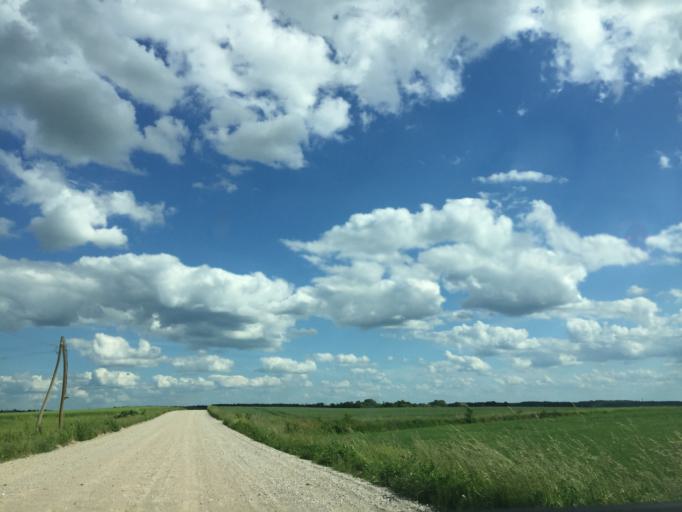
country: LV
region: Jaunpils
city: Jaunpils
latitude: 56.8380
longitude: 23.0436
